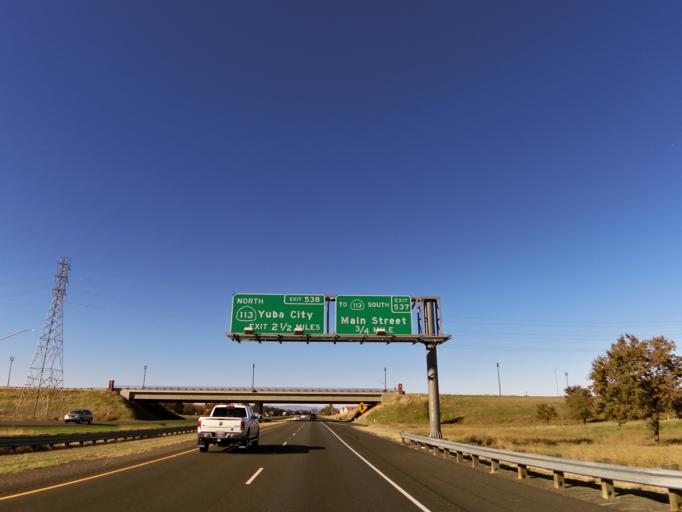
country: US
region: California
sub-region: Yolo County
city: Woodland
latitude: 38.6739
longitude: -121.7270
